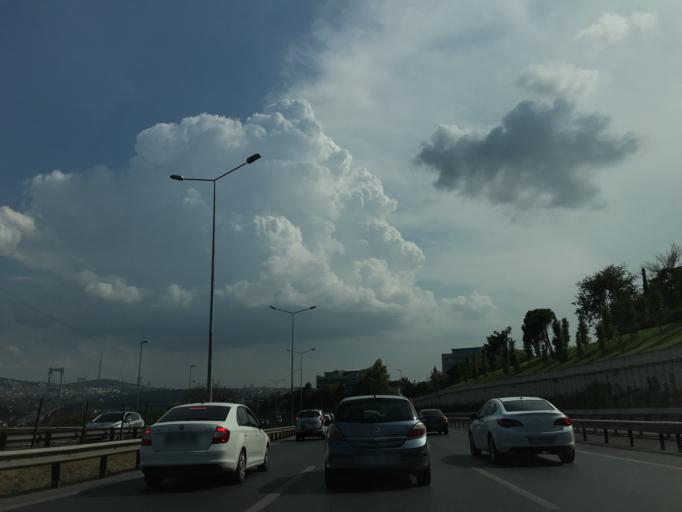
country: TR
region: Istanbul
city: Sisli
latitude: 41.0607
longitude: 29.0160
